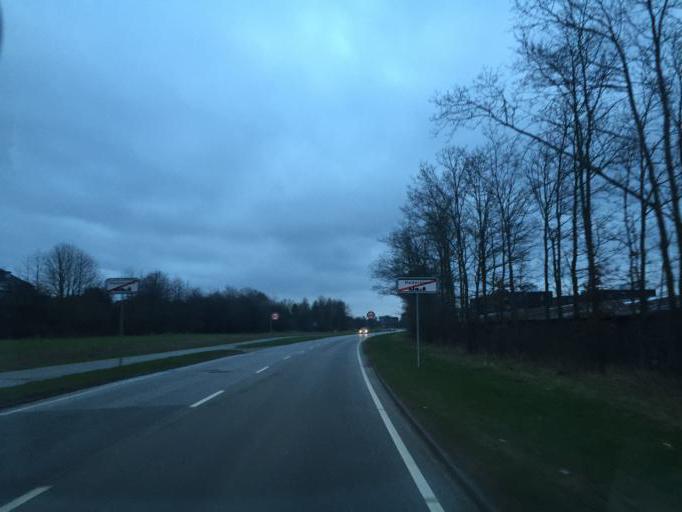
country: DK
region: South Denmark
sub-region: Haderslev Kommune
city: Haderslev
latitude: 55.2533
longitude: 9.5082
